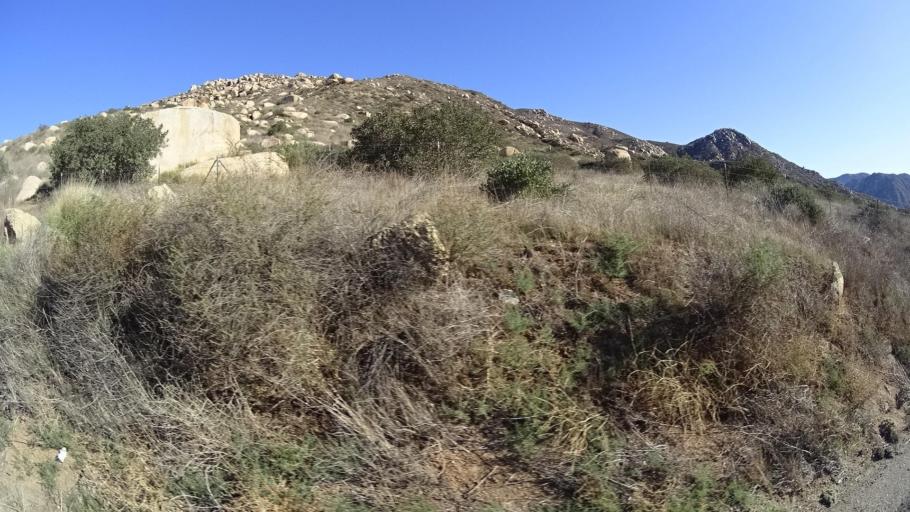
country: MX
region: Baja California
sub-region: Tecate
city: Lomas de Santa Anita
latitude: 32.6143
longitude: -116.7148
